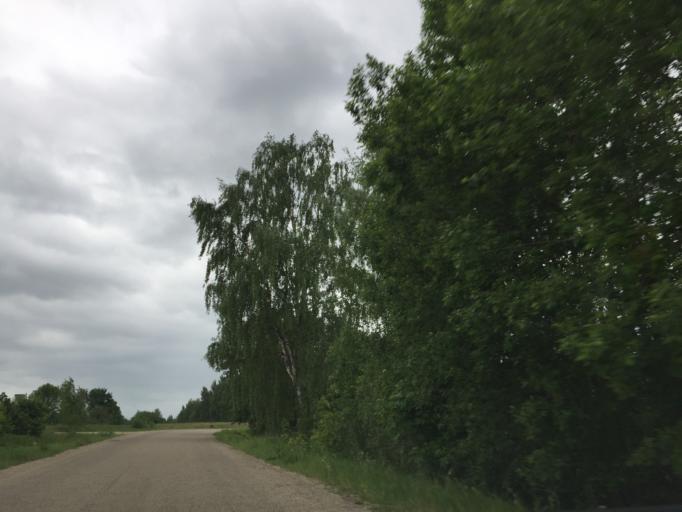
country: LV
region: Aglona
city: Aglona
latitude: 56.0753
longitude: 26.9044
